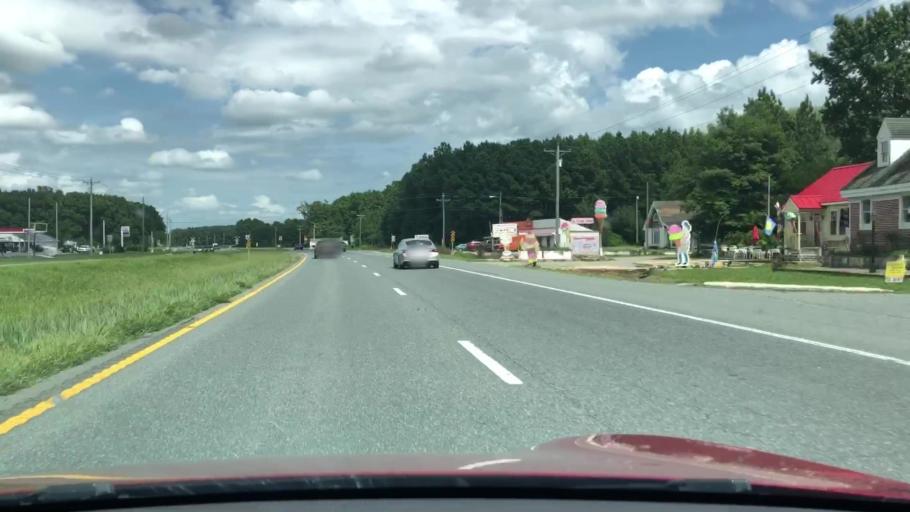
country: US
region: Virginia
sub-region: Accomack County
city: Accomac
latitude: 37.7057
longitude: -75.6987
